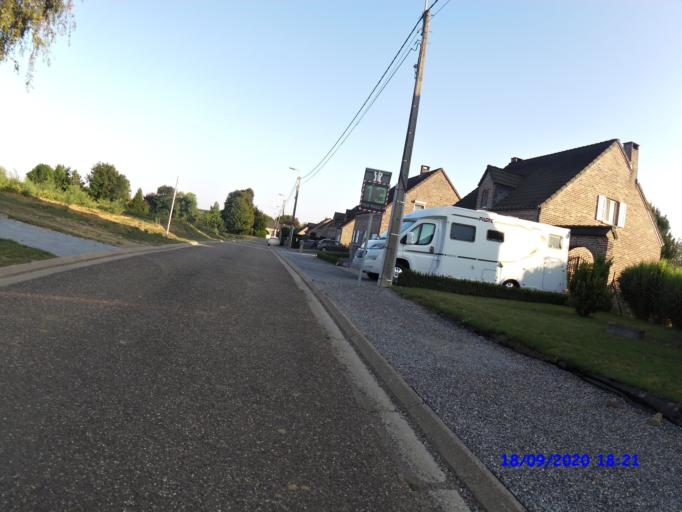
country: BE
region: Wallonia
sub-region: Province de Liege
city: Berloz
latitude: 50.6991
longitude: 5.2223
